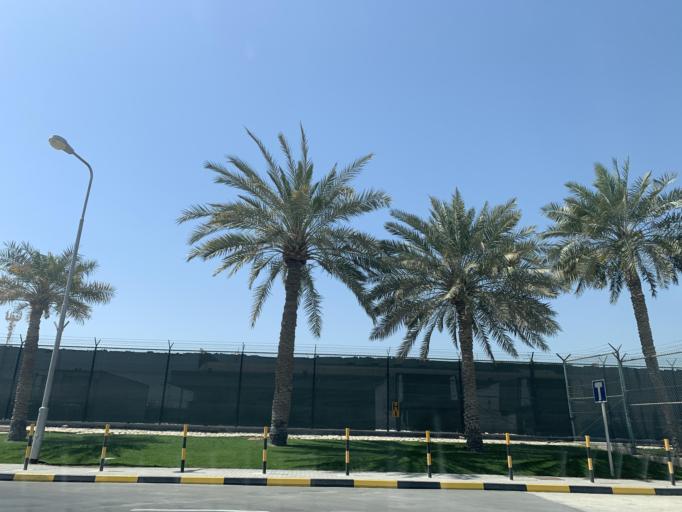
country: BH
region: Muharraq
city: Al Muharraq
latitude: 26.2714
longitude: 50.6225
